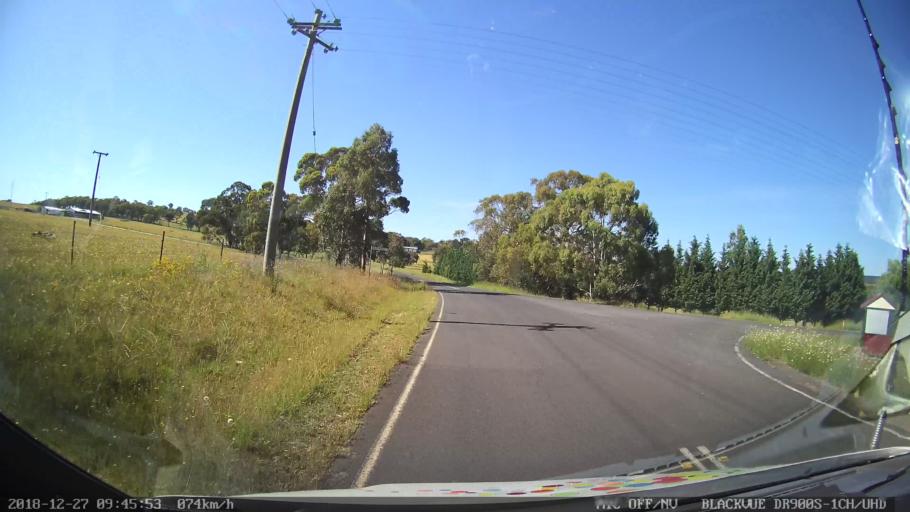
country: AU
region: New South Wales
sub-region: Lithgow
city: Portland
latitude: -33.3296
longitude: 149.9837
